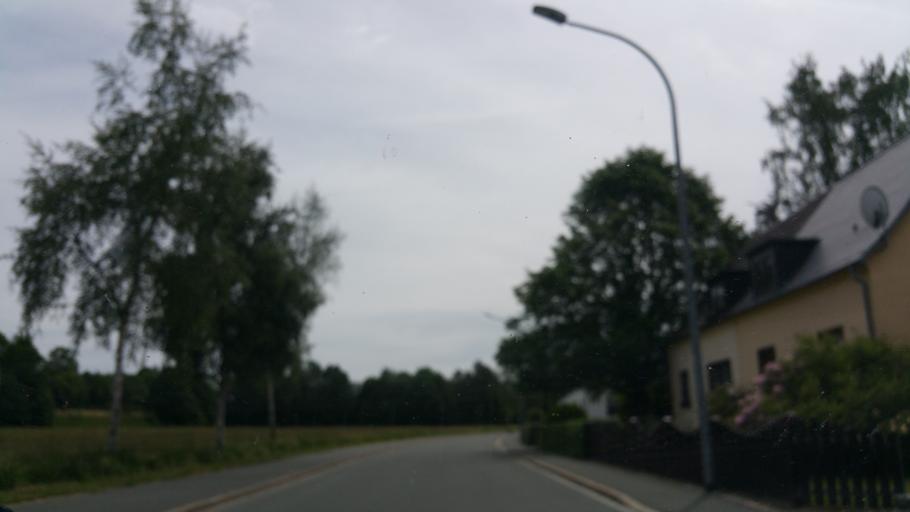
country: DE
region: Bavaria
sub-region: Upper Franconia
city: Rehau
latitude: 50.2435
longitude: 12.0270
